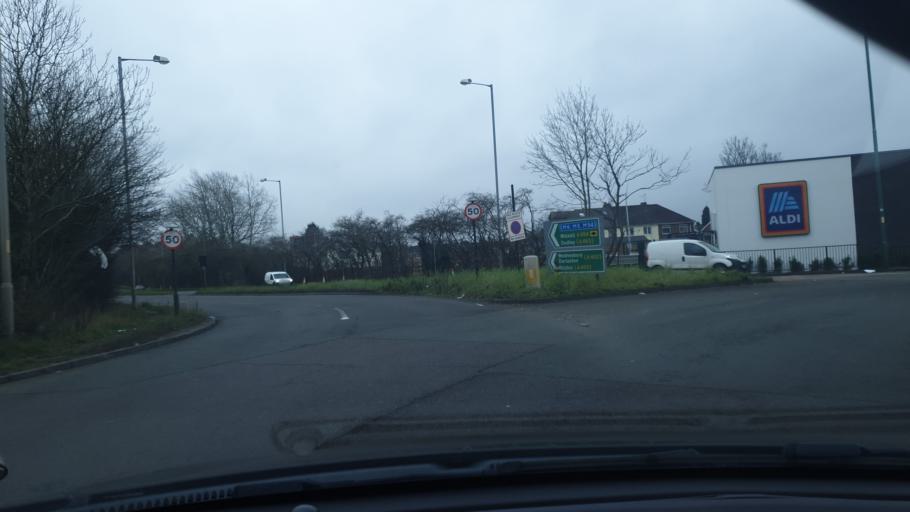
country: GB
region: England
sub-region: Walsall
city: Willenhall
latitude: 52.5825
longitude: -2.0668
